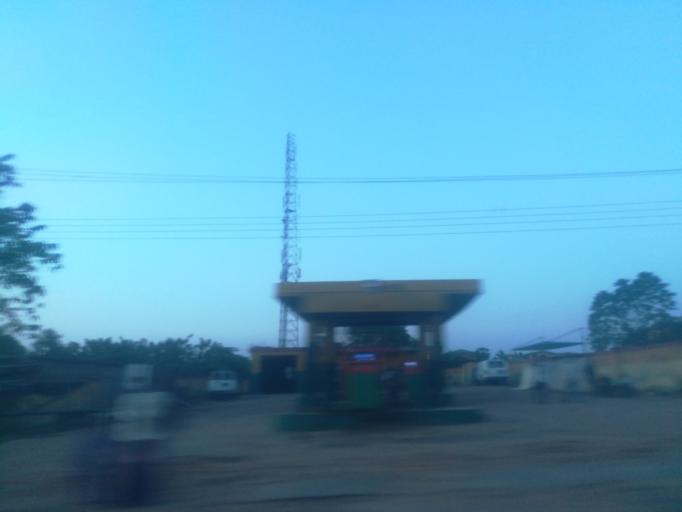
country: NG
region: Ogun
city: Abeokuta
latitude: 7.1800
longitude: 3.4120
